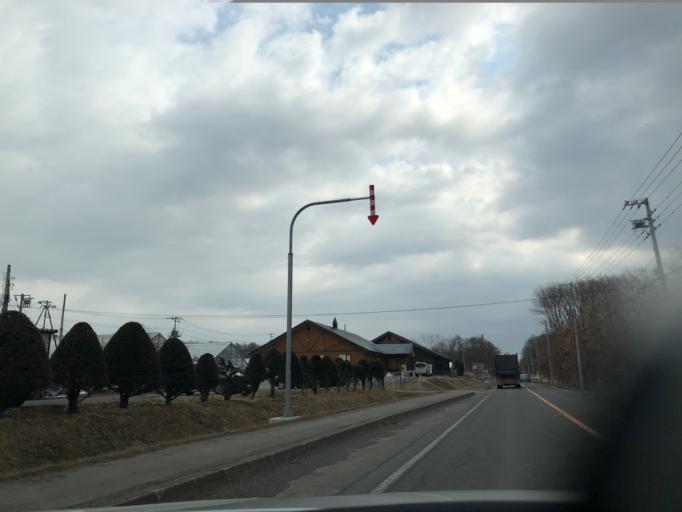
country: JP
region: Hokkaido
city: Chitose
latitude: 42.7604
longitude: 141.7823
